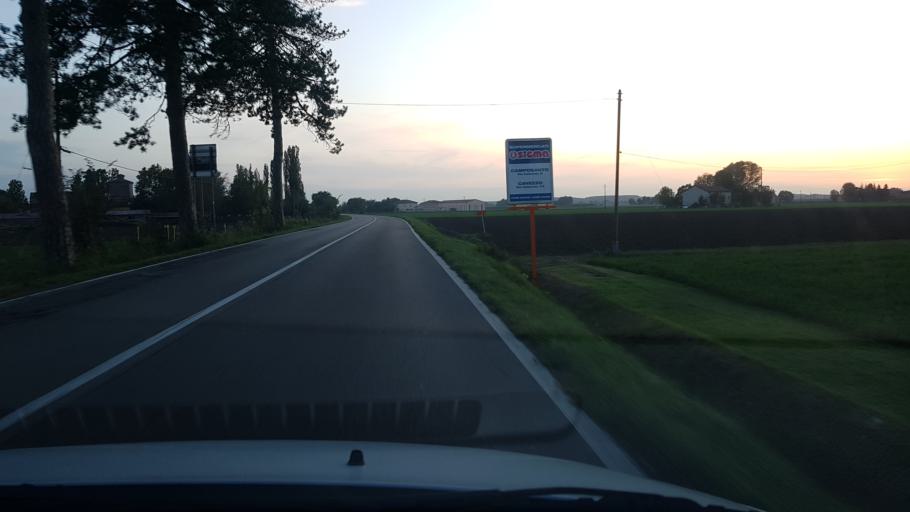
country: IT
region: Emilia-Romagna
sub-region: Provincia di Modena
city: Cavezzo
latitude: 44.8204
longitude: 11.0413
